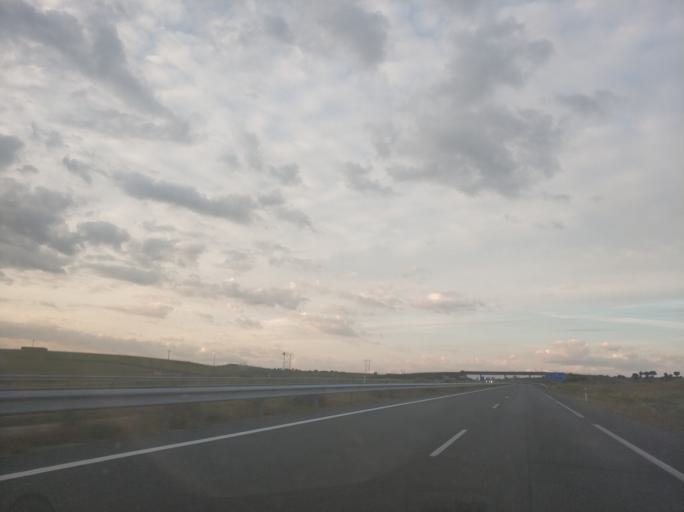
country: ES
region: Castille and Leon
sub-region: Provincia de Salamanca
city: Montejo
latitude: 40.6422
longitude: -5.6310
